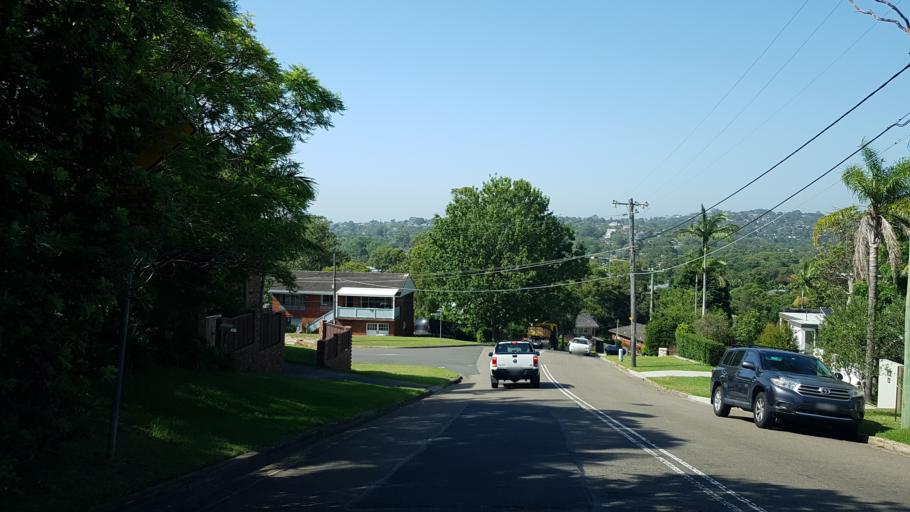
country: AU
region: New South Wales
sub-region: Warringah
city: Narrabeen
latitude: -33.7294
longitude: 151.2796
